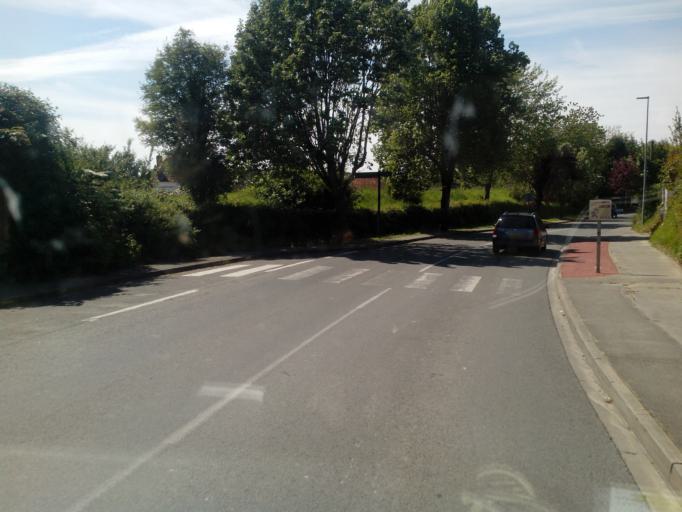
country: FR
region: Nord-Pas-de-Calais
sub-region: Departement du Pas-de-Calais
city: Montreuil
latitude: 50.4872
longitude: 1.7446
